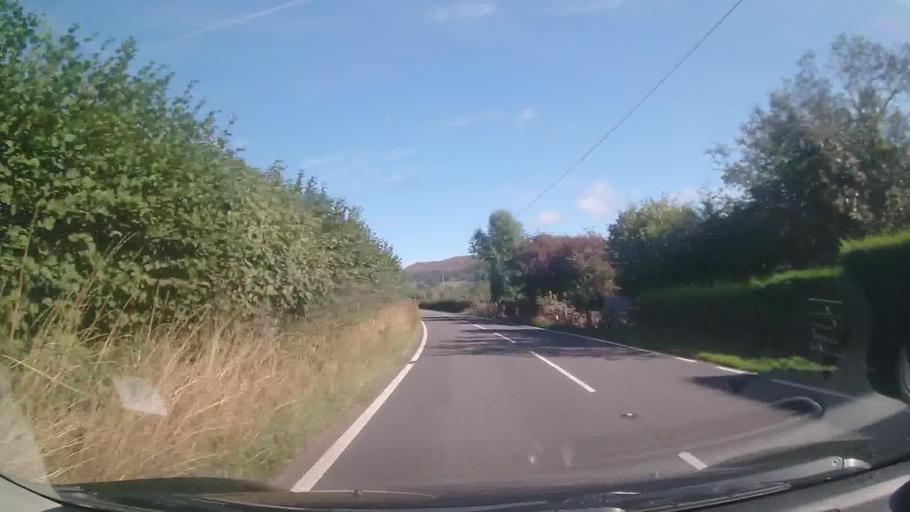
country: GB
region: Wales
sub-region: Blaenau Gwent
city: Brynmawr
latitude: 51.9326
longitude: -3.1877
